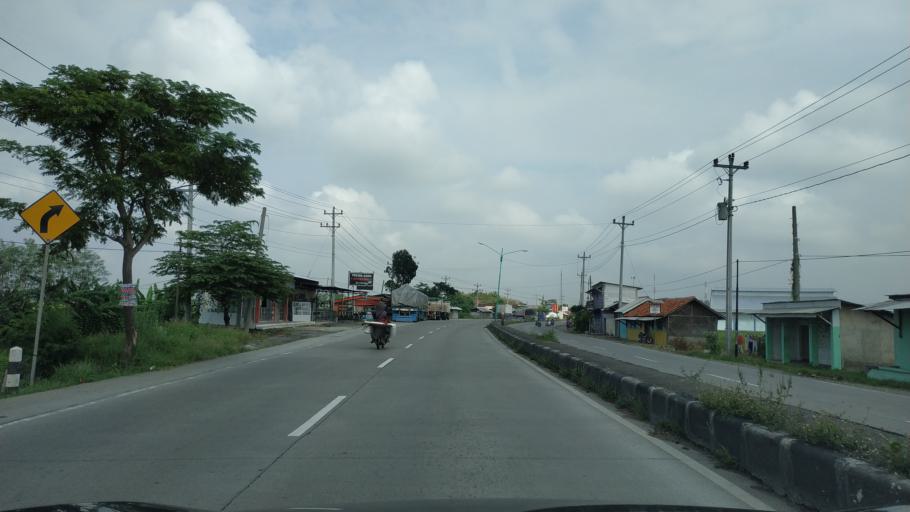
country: ID
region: Central Java
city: Bulakamba
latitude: -6.8754
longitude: 108.9546
